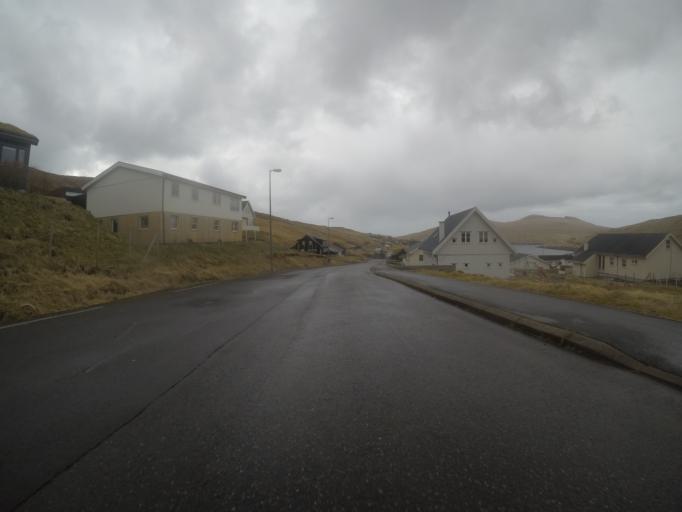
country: FO
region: Vagar
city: Midvagur
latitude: 62.0608
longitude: -7.1450
